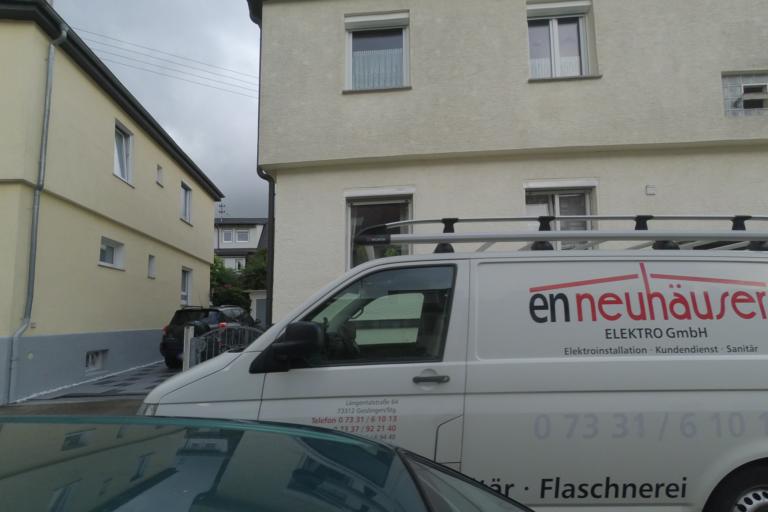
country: DE
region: Baden-Wuerttemberg
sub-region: Regierungsbezirk Stuttgart
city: Geislingen an der Steige
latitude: 48.6246
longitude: 9.8377
